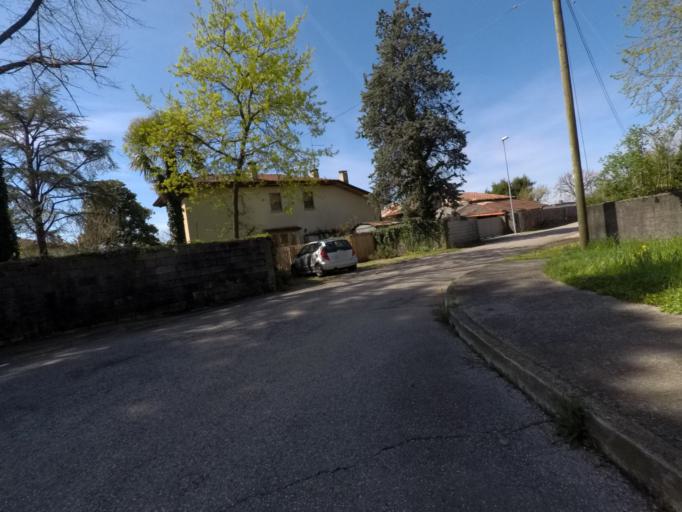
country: IT
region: Friuli Venezia Giulia
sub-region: Provincia di Udine
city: Codroipo
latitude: 45.9555
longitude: 12.9739
